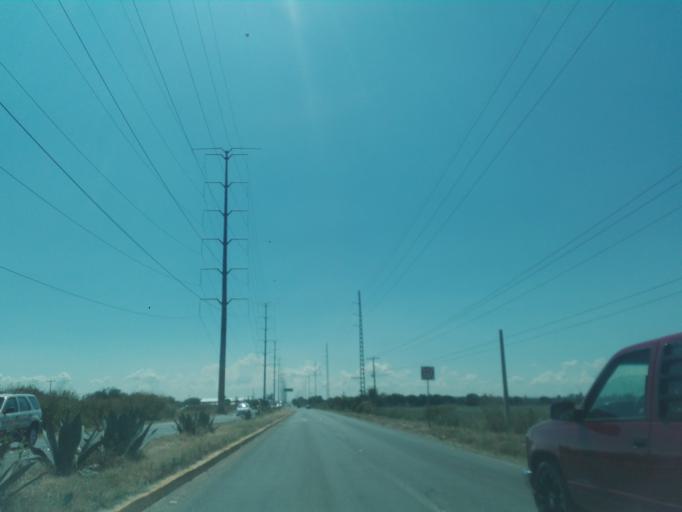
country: MX
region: Guanajuato
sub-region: Leon
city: San Antonio de los Tepetates
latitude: 21.0461
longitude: -101.6906
